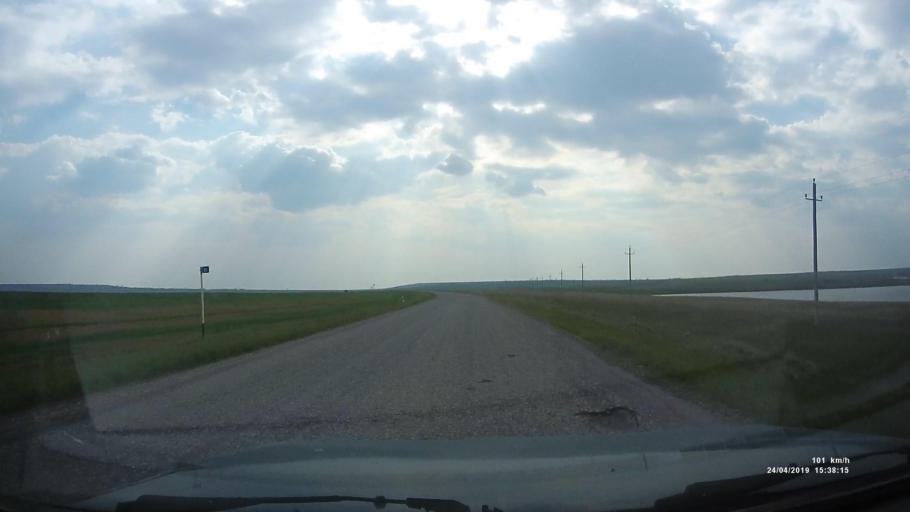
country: RU
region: Kalmykiya
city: Yashalta
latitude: 46.5992
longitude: 42.8313
